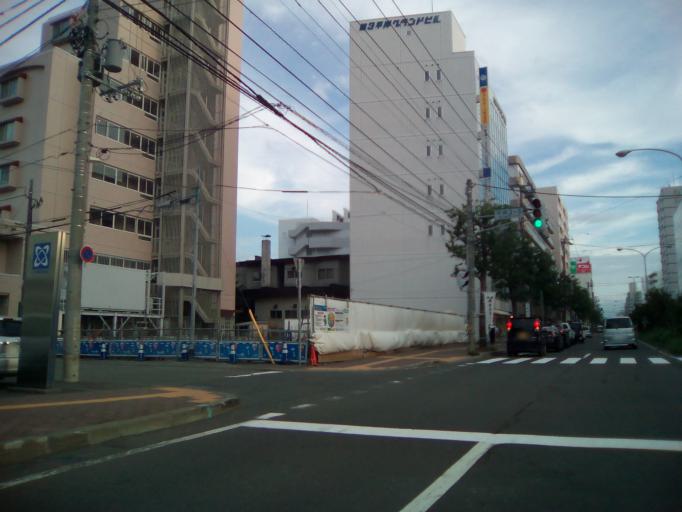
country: JP
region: Hokkaido
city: Sapporo
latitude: 43.0381
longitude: 141.3697
